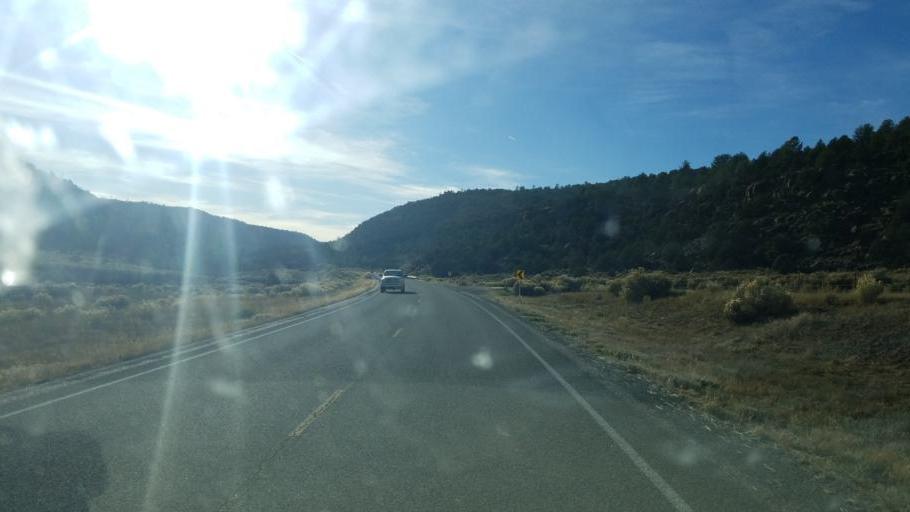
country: US
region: New Mexico
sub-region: Rio Arriba County
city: Navajo
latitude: 36.7422
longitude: -107.2340
